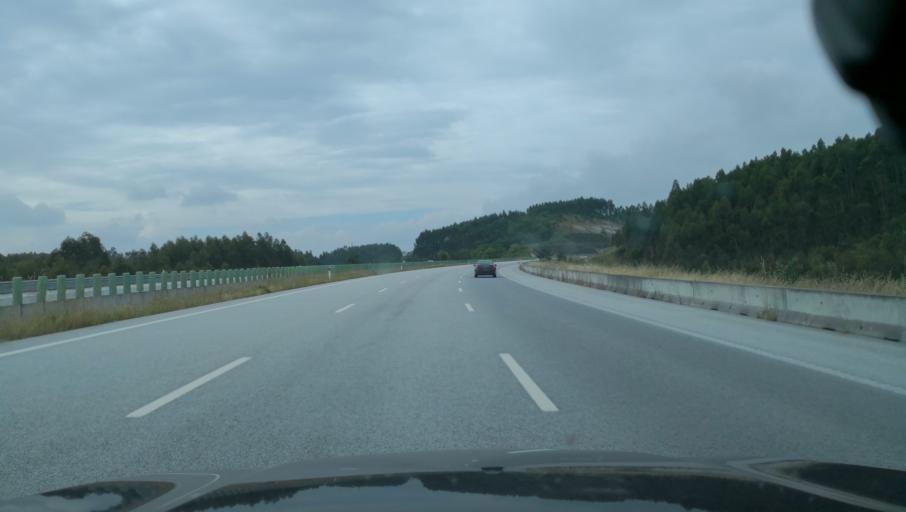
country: PT
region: Coimbra
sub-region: Montemor-O-Velho
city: Montemor-o-Velho
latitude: 40.1102
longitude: -8.7438
